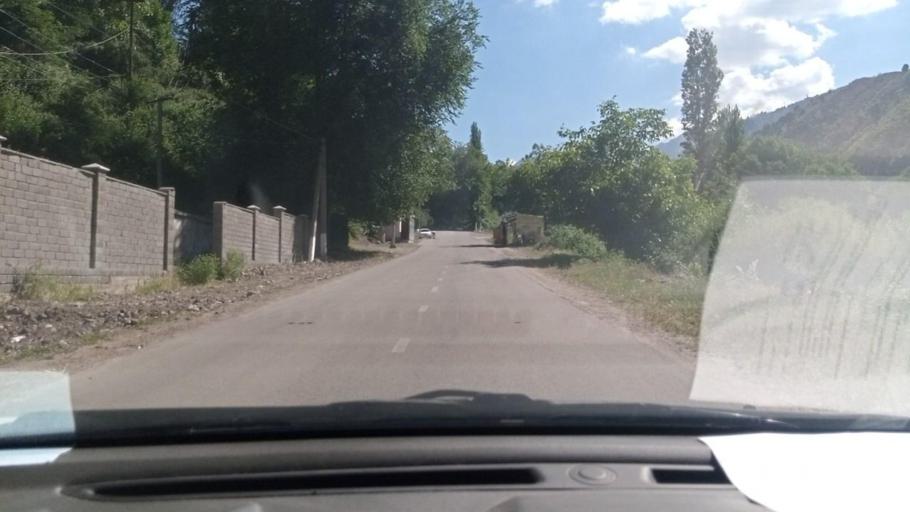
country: UZ
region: Toshkent
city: Yangiobod
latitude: 41.1156
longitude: 70.0904
